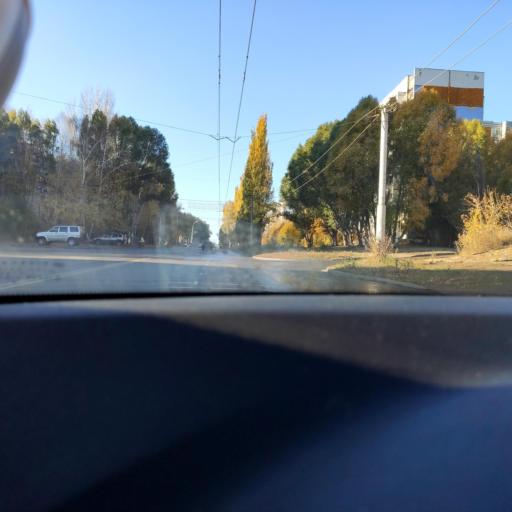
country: RU
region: Samara
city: Samara
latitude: 53.2521
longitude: 50.2559
